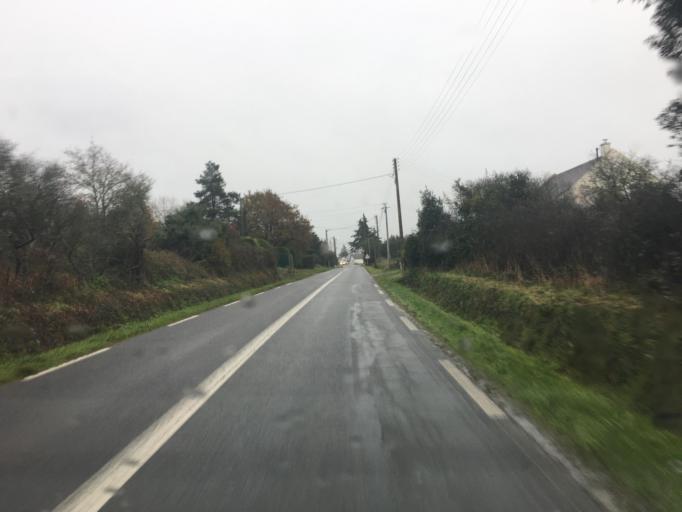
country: FR
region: Pays de la Loire
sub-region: Departement de la Loire-Atlantique
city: La Turballe
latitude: 47.3393
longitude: -2.4710
